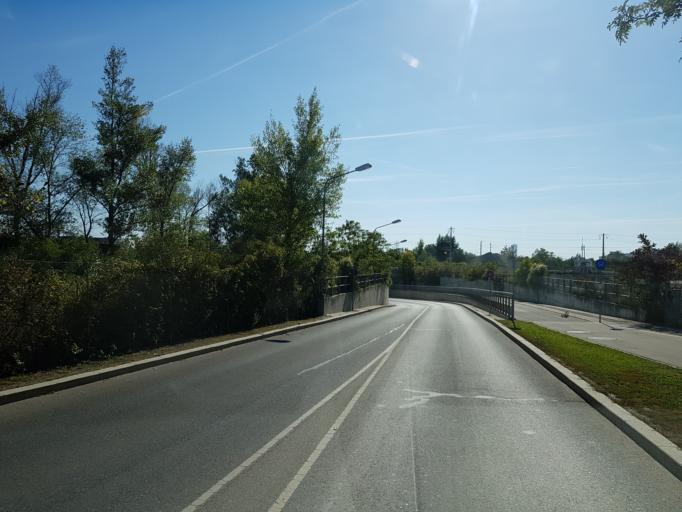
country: AT
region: Lower Austria
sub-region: Politischer Bezirk Wien-Umgebung
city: Gerasdorf bei Wien
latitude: 48.2753
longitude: 16.4320
